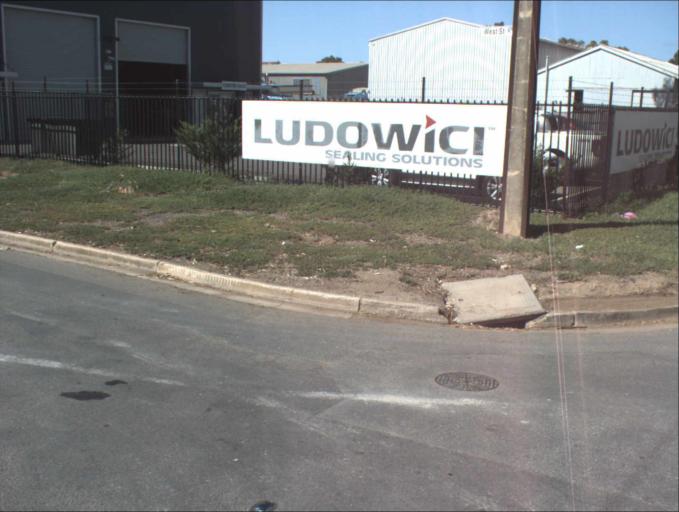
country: AU
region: South Australia
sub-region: Charles Sturt
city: Woodville North
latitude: -34.8393
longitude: 138.5517
